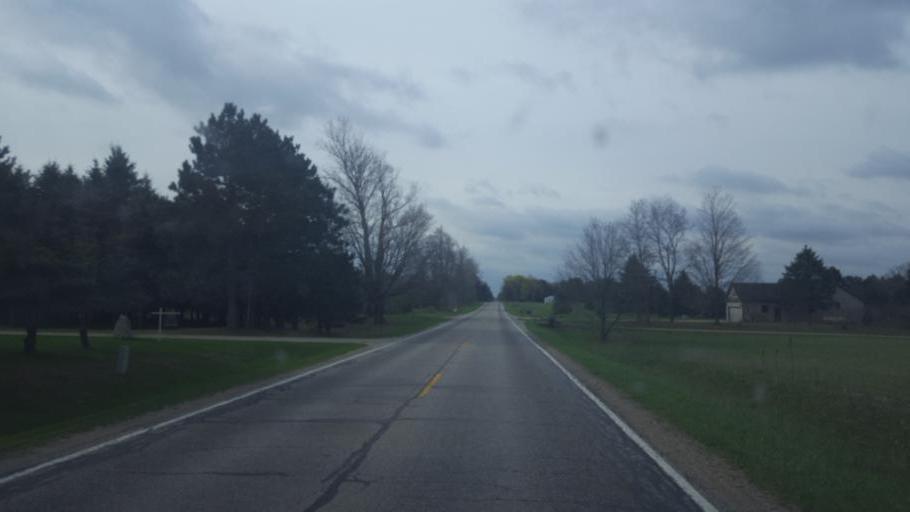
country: US
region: Michigan
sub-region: Isabella County
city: Lake Isabella
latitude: 43.5466
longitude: -84.9866
